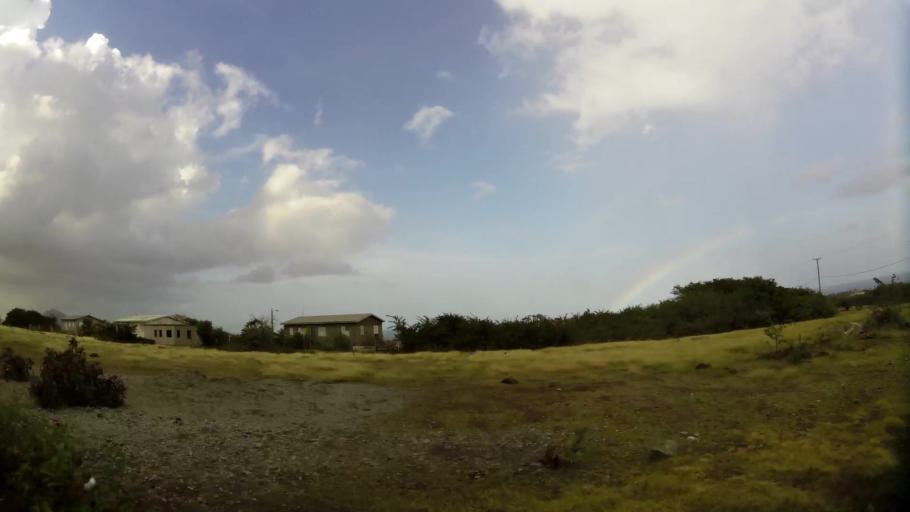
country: KN
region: Saint James Windwa
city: Newcastle
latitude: 17.1954
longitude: -62.5812
